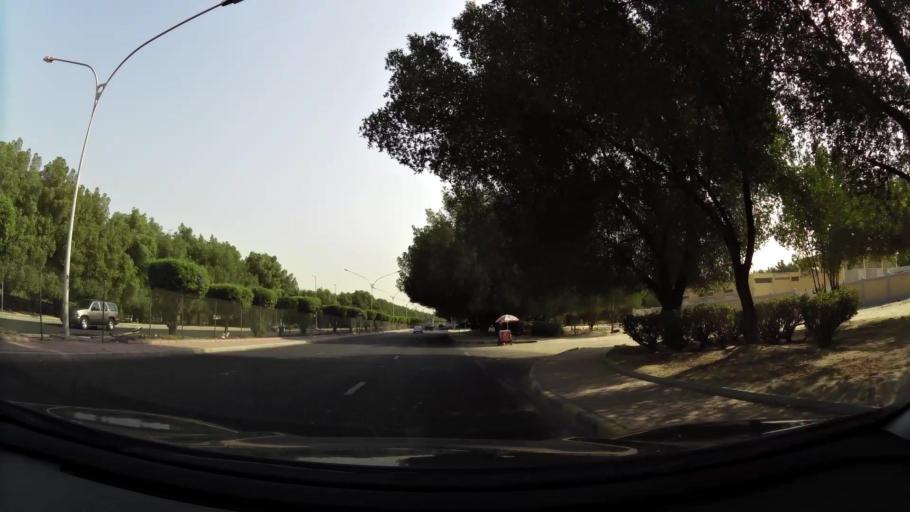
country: KW
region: Muhafazat Hawalli
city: Salwa
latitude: 29.2804
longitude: 48.0622
